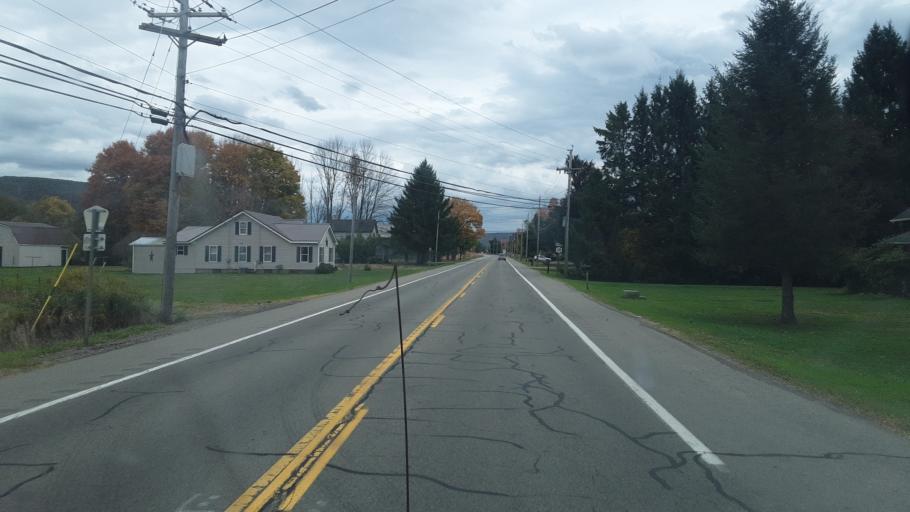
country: US
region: New York
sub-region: Allegany County
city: Belmont
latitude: 42.2087
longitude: -78.0140
